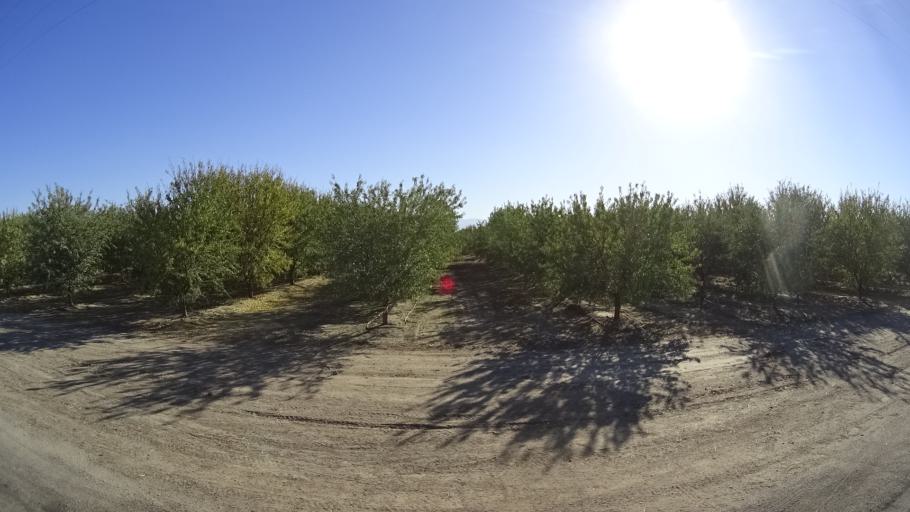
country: US
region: California
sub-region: Kern County
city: Greenacres
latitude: 35.2813
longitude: -119.1252
